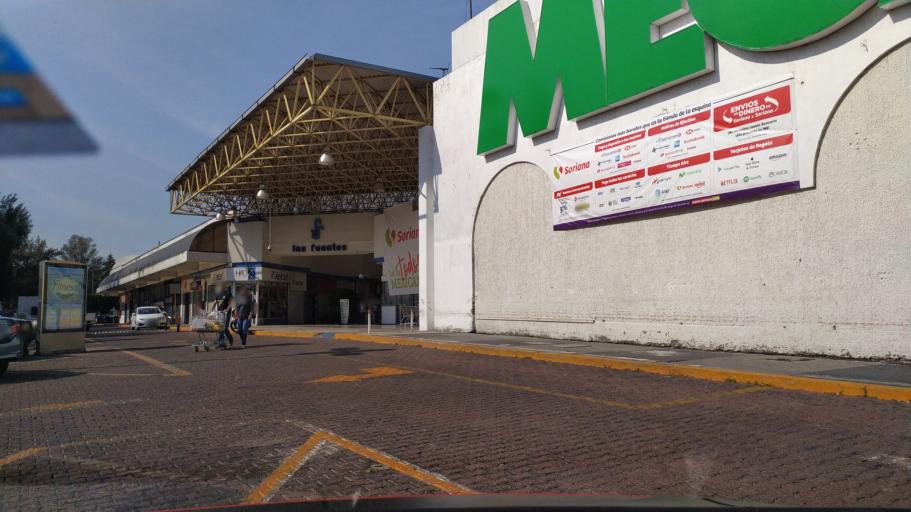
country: MX
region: Jalisco
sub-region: Tlajomulco de Zuniga
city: La Tijera
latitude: 20.6181
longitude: -103.4225
